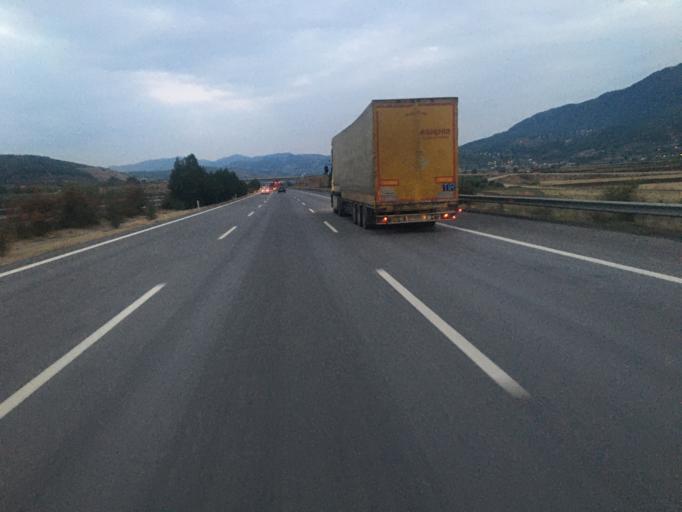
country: TR
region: Osmaniye
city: Osmaniye
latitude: 37.1456
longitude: 36.3332
